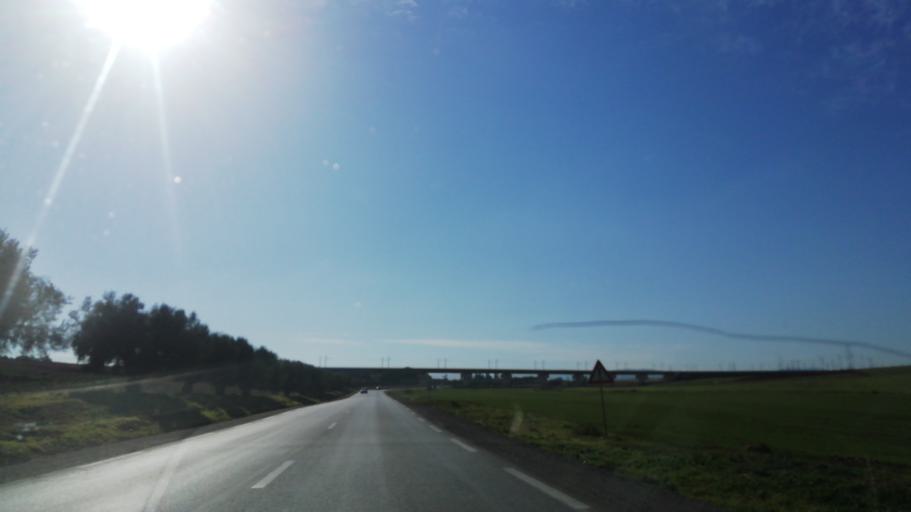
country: DZ
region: Tlemcen
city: Ouled Mimoun
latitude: 35.0113
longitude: -0.9060
